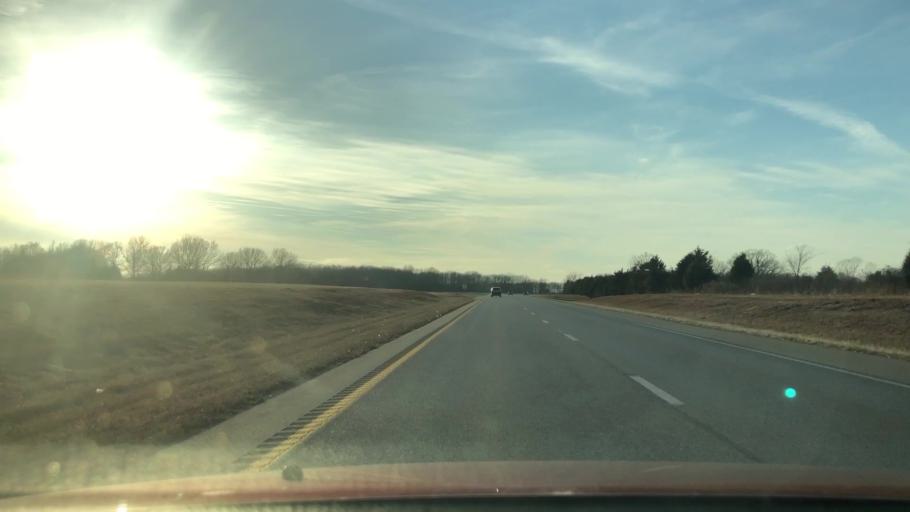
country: US
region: Missouri
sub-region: Webster County
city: Seymour
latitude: 37.1309
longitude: -92.7272
